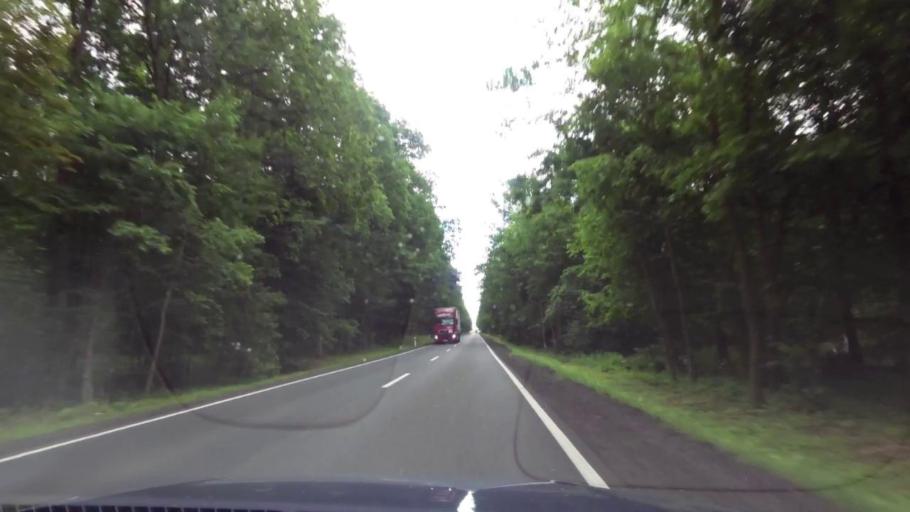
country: PL
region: West Pomeranian Voivodeship
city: Trzcinsko Zdroj
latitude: 52.9704
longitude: 14.7375
